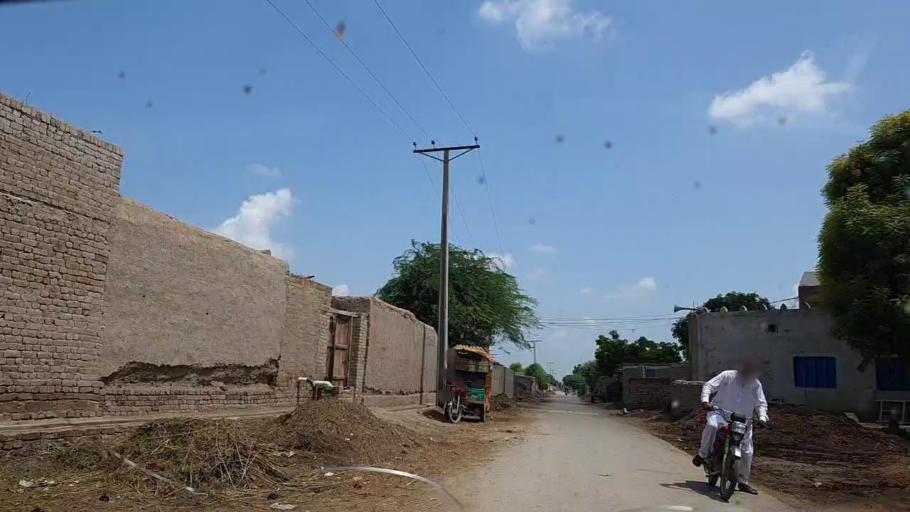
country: PK
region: Sindh
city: Tharu Shah
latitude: 26.9631
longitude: 68.0978
